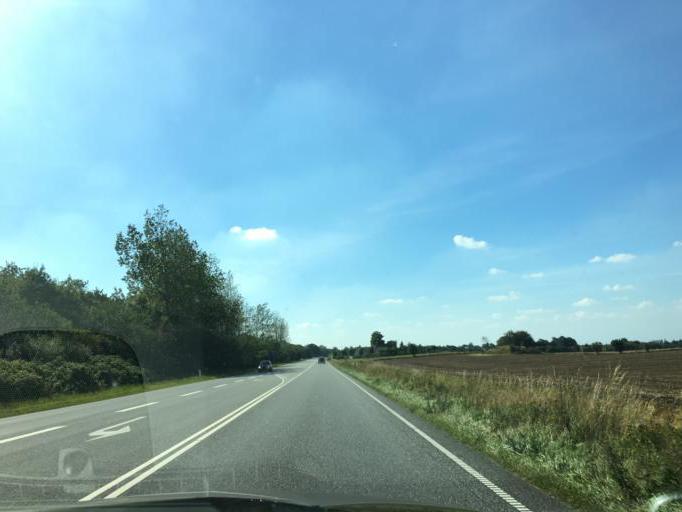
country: DK
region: South Denmark
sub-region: Kolding Kommune
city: Lunderskov
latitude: 55.4923
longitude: 9.2964
